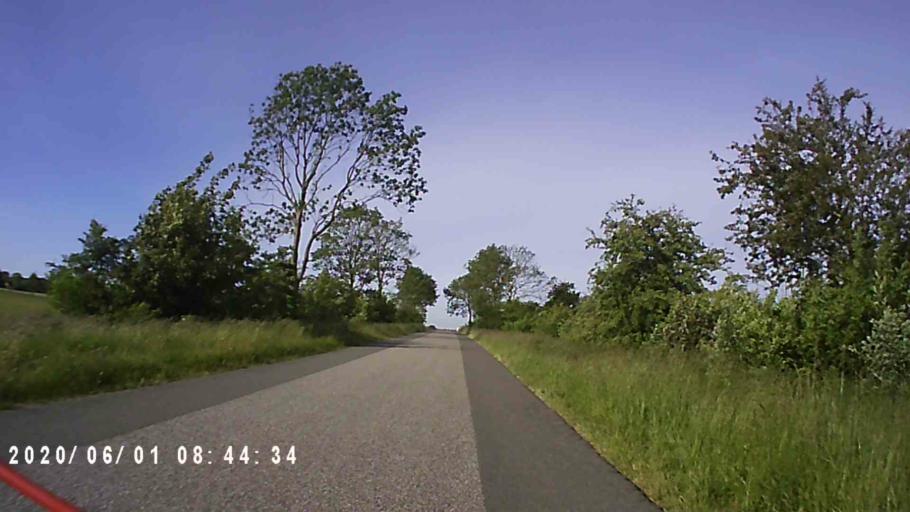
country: NL
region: Friesland
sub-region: Gemeente Ferwerderadiel
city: Burdaard
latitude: 53.2799
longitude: 5.8374
